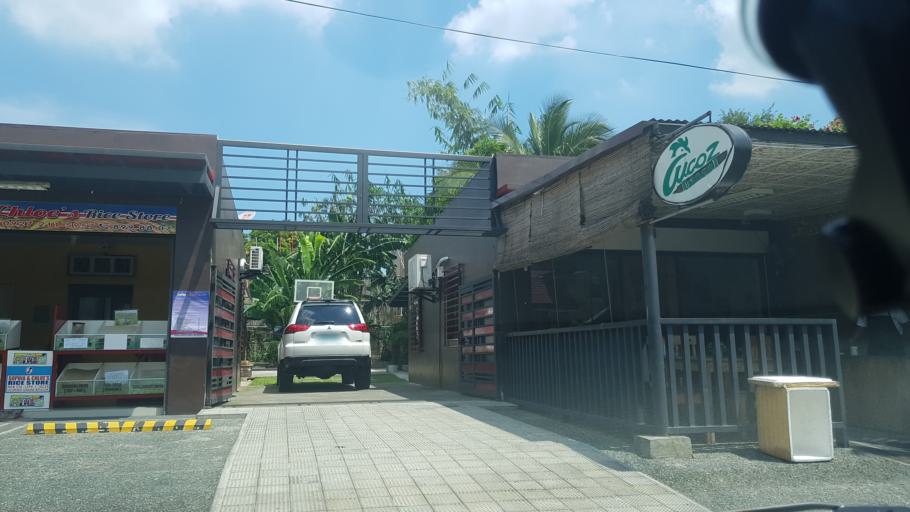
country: PH
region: Calabarzon
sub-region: Province of Rizal
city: Las Pinas
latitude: 14.4266
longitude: 120.9937
